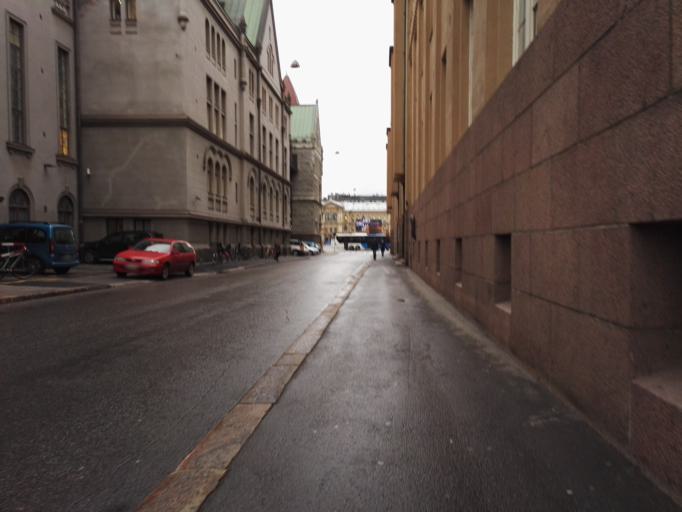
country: FI
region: Uusimaa
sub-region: Helsinki
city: Helsinki
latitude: 60.1728
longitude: 24.9433
